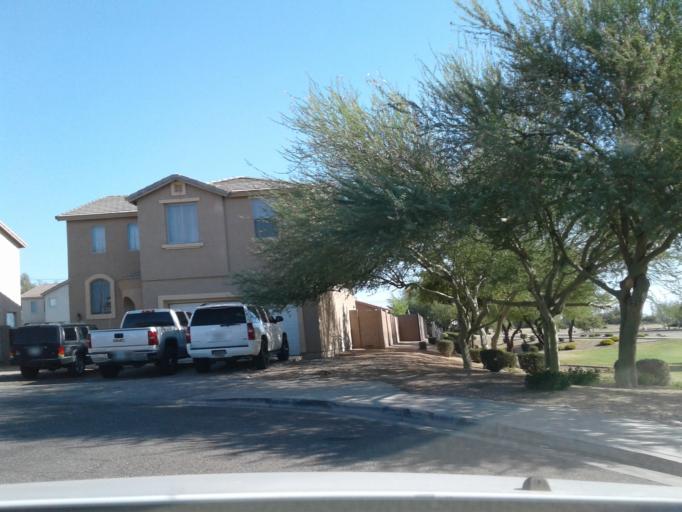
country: US
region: Arizona
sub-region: Maricopa County
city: Laveen
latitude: 33.4140
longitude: -112.1884
